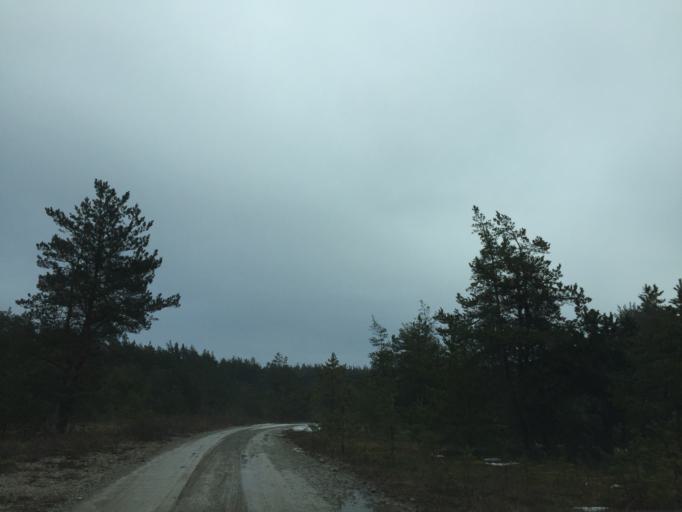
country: EE
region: Saare
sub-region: Orissaare vald
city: Orissaare
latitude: 58.6142
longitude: 22.9480
